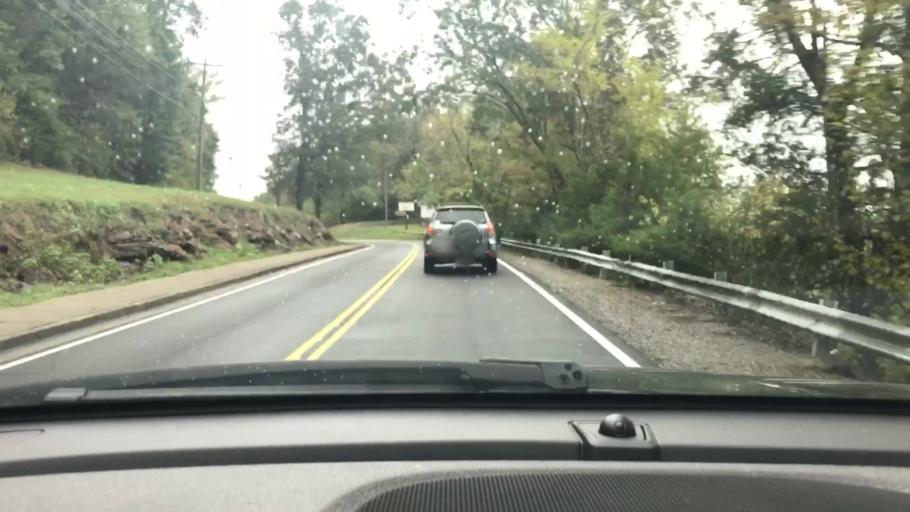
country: US
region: Tennessee
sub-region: Cheatham County
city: Kingston Springs
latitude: 36.0934
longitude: -87.1105
